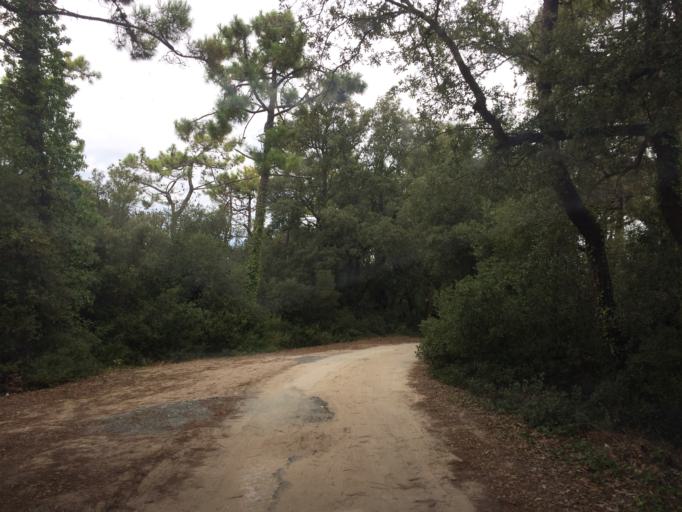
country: FR
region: Poitou-Charentes
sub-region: Departement de la Charente-Maritime
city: La Couarde-sur-Mer
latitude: 46.1995
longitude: -1.4498
